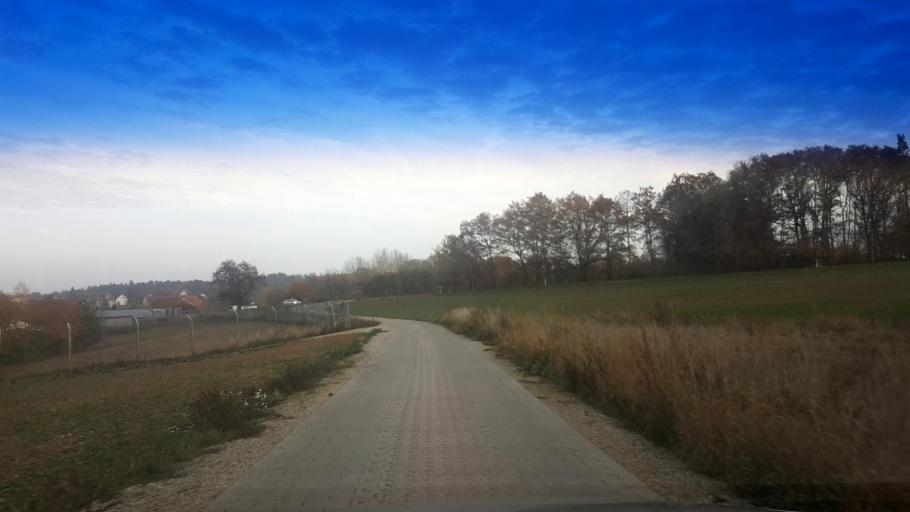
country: DE
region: Bavaria
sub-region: Upper Franconia
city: Viereth-Trunstadt
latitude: 49.9021
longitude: 10.7657
